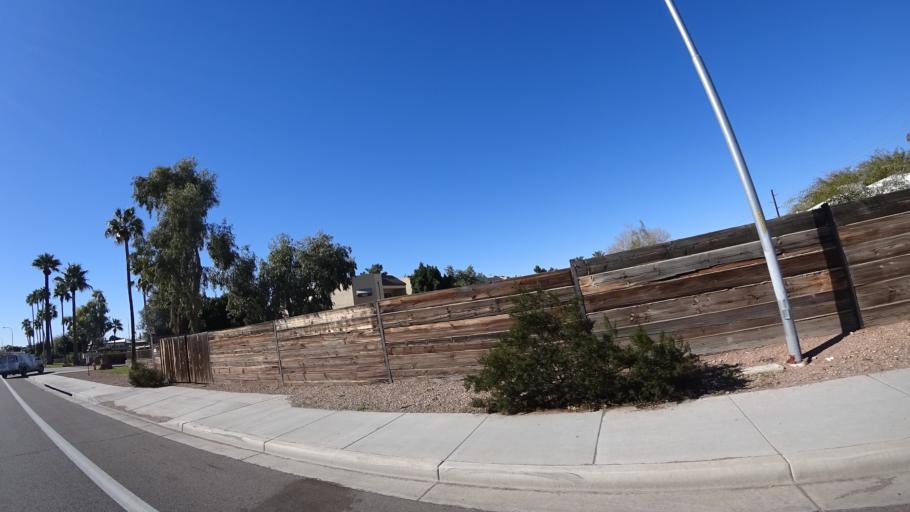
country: US
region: Arizona
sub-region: Maricopa County
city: Tempe Junction
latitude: 33.4723
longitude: -111.9697
